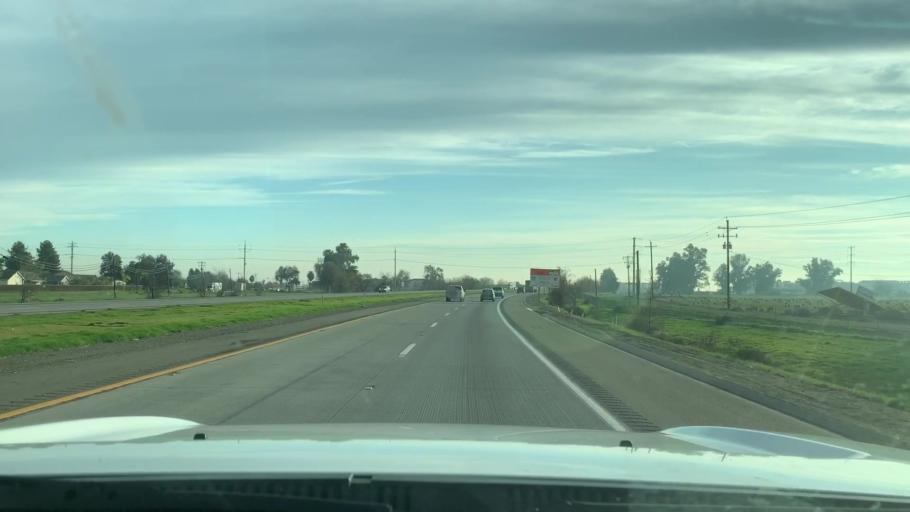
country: US
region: California
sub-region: Kings County
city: Lemoore
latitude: 36.3081
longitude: -119.8083
